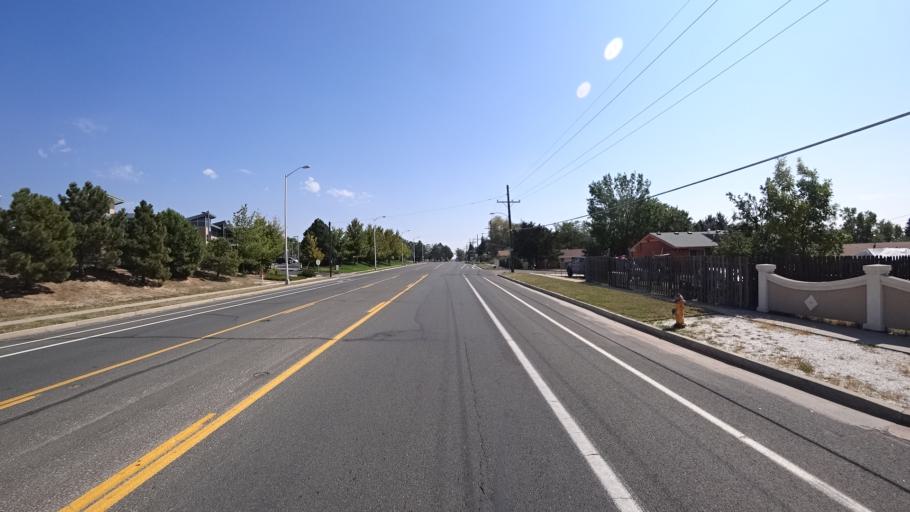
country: US
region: Colorado
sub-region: El Paso County
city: Colorado Springs
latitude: 38.8253
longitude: -104.7887
